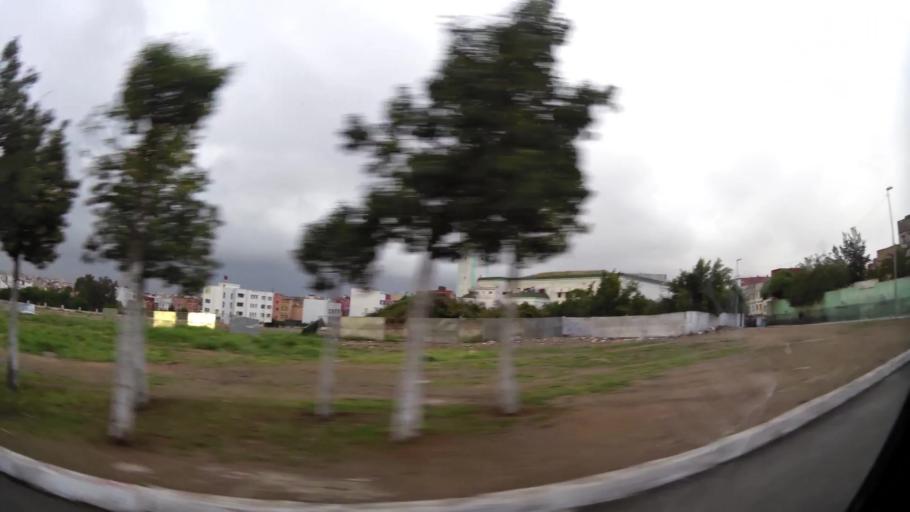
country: MA
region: Grand Casablanca
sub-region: Casablanca
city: Casablanca
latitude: 33.5538
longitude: -7.5818
